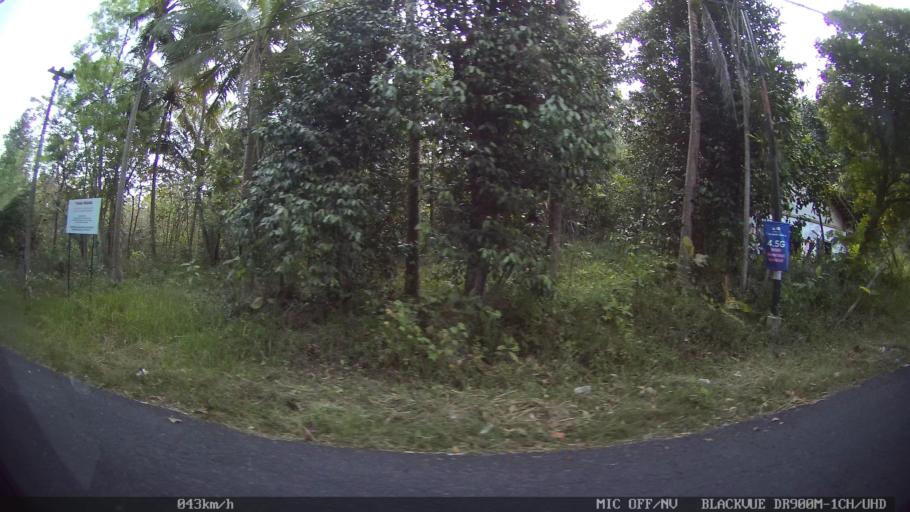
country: ID
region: Daerah Istimewa Yogyakarta
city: Bantul
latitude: -7.8607
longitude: 110.3195
